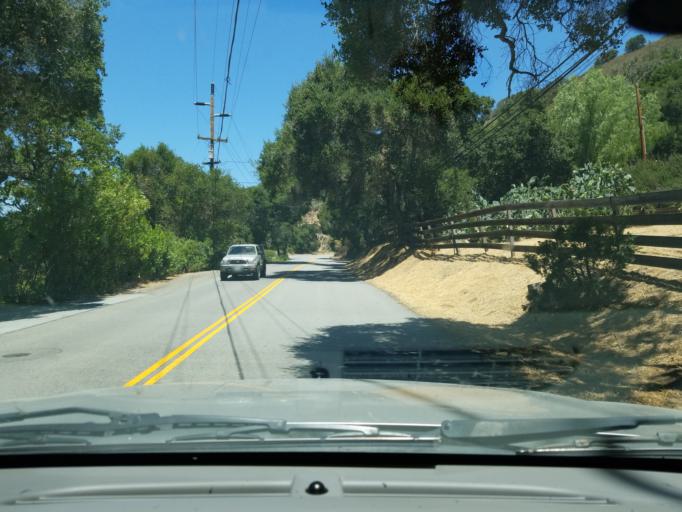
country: US
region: California
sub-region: Monterey County
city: Carmel Valley Village
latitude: 36.4673
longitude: -121.7128
